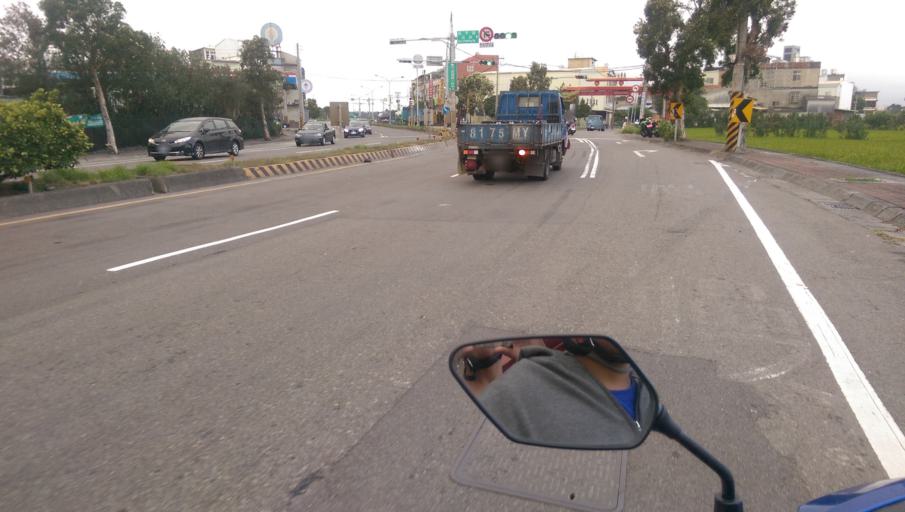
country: TW
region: Taiwan
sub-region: Hsinchu
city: Hsinchu
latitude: 24.8268
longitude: 120.9277
